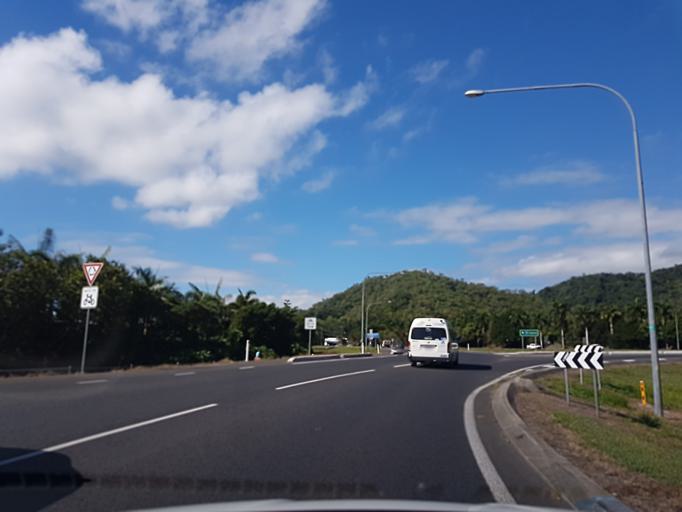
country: AU
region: Queensland
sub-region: Cairns
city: Trinity Beach
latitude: -16.7925
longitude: 145.6792
